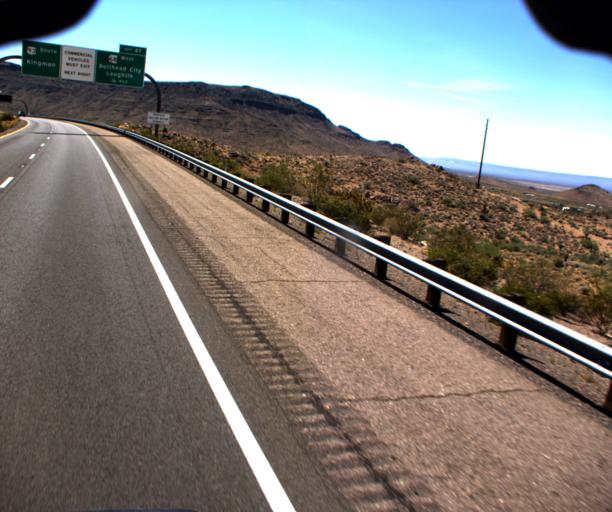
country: US
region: Arizona
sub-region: Mohave County
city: Golden Valley
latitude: 35.2305
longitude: -114.1365
